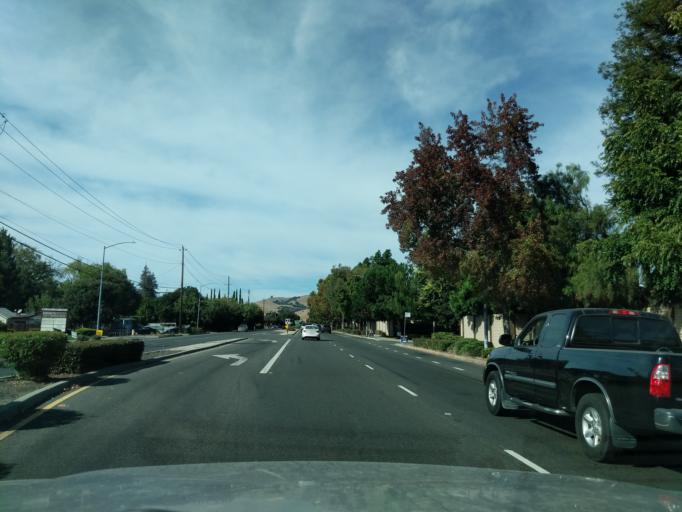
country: US
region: California
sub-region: Alameda County
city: Fremont
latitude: 37.5626
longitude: -121.9588
